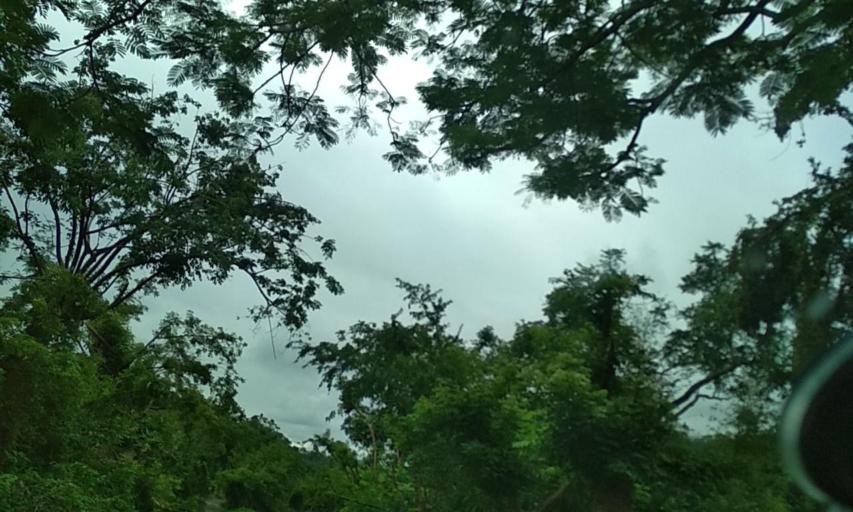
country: MX
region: Veracruz
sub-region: Papantla
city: Residencial Tajin
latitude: 20.6064
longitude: -97.3357
